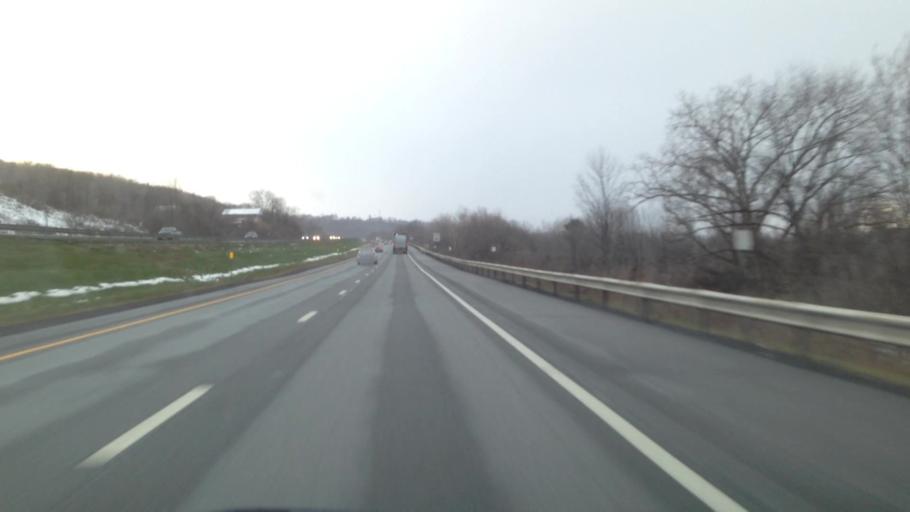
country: US
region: New York
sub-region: Montgomery County
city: Saint Johnsville
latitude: 42.9907
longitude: -74.6931
